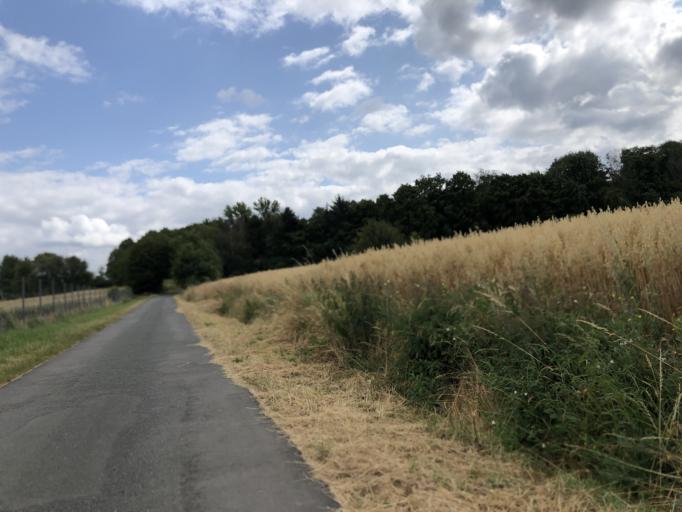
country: DE
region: North Rhine-Westphalia
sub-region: Regierungsbezirk Detmold
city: Detmold
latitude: 51.9372
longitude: 8.8413
